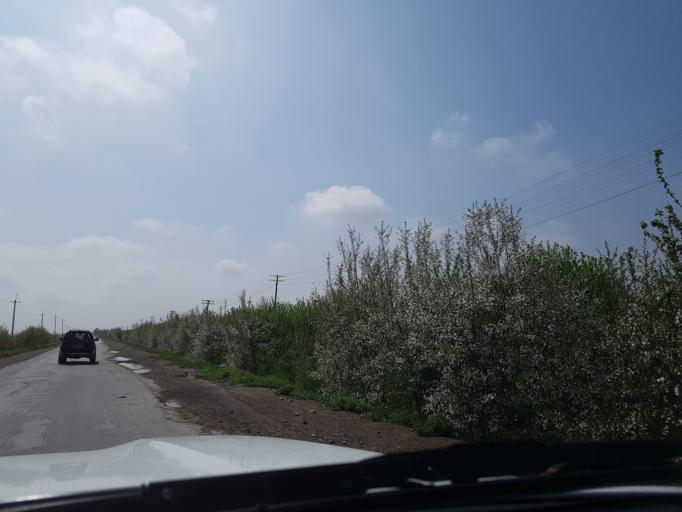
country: TM
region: Lebap
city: Turkmenabat
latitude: 38.9633
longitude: 63.6789
